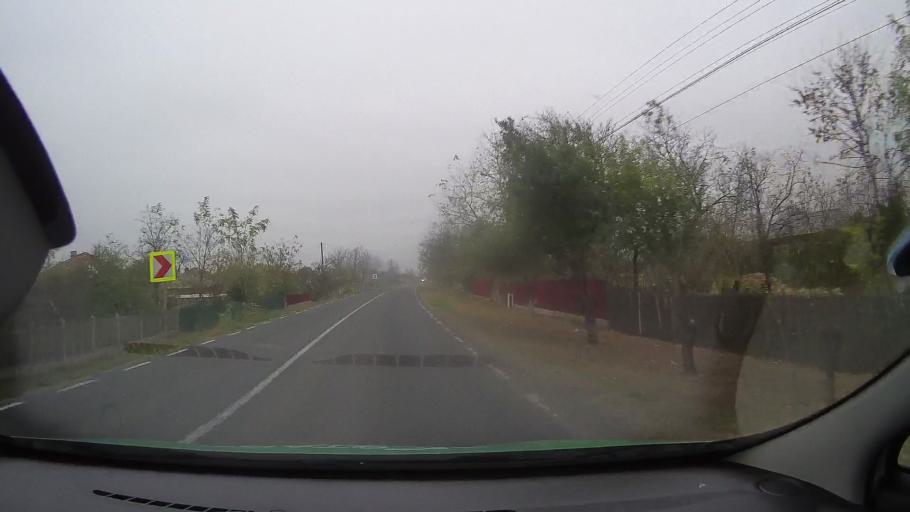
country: RO
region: Braila
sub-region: Comuna Baraganul
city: Baraganul
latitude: 44.8004
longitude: 27.5132
